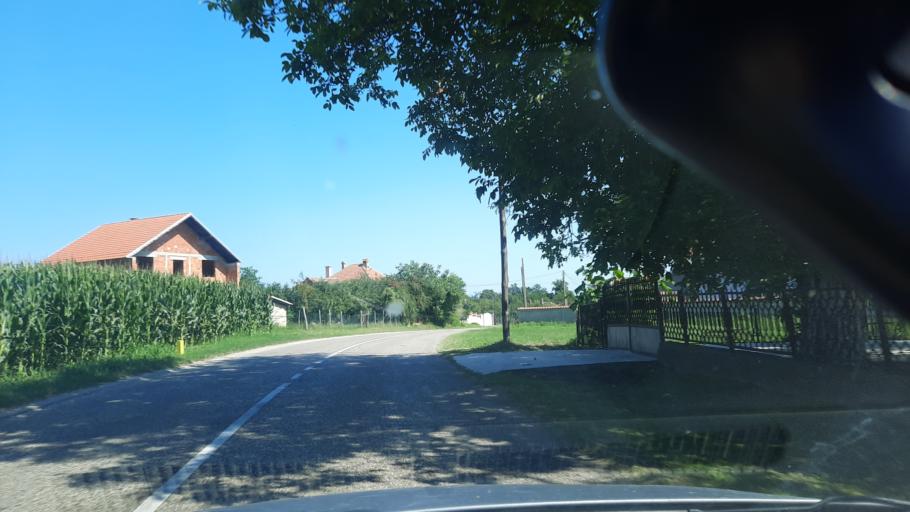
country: RS
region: Central Serbia
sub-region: Branicevski Okrug
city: Malo Crnice
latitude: 44.5906
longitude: 21.2742
